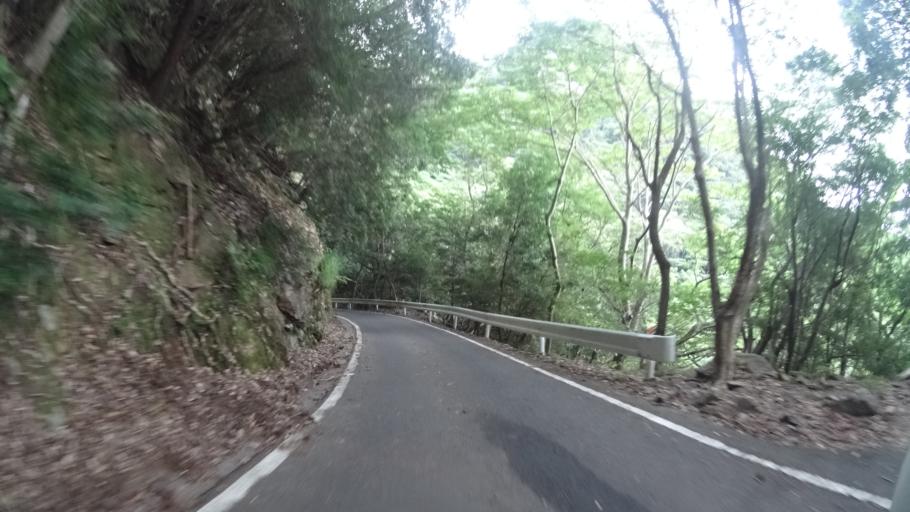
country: JP
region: Kagoshima
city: Nishinoomote
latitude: 30.3328
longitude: 130.3967
